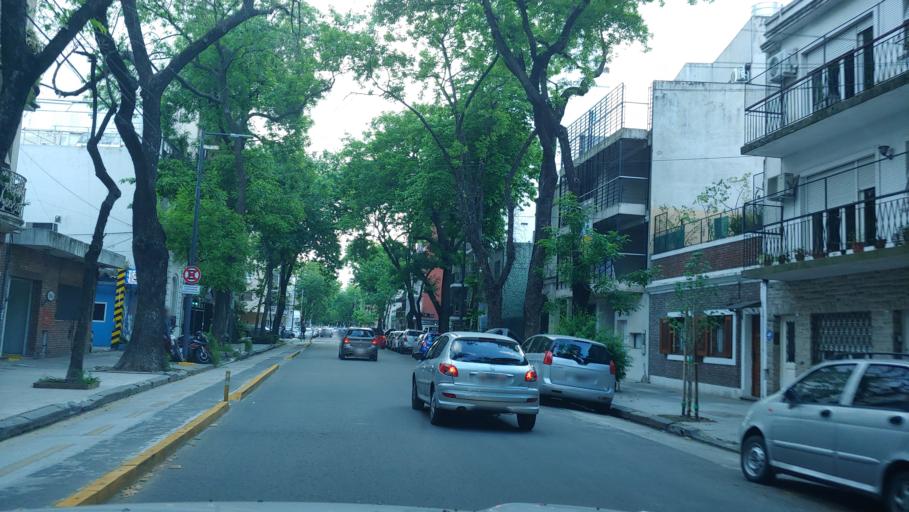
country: AR
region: Buenos Aires F.D.
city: Colegiales
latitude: -34.5722
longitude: -58.4450
